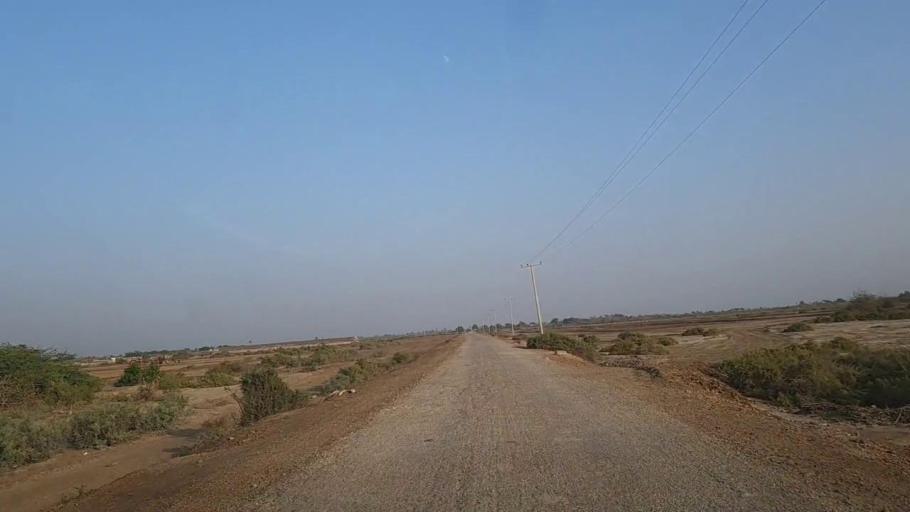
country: PK
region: Sindh
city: Keti Bandar
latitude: 24.2796
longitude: 67.6307
